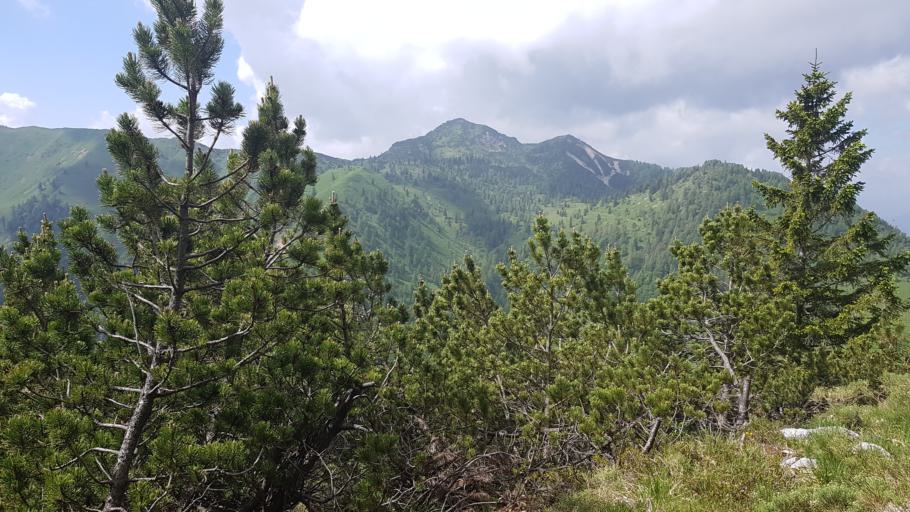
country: IT
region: Friuli Venezia Giulia
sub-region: Provincia di Udine
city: Paularo
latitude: 46.5339
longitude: 13.1905
